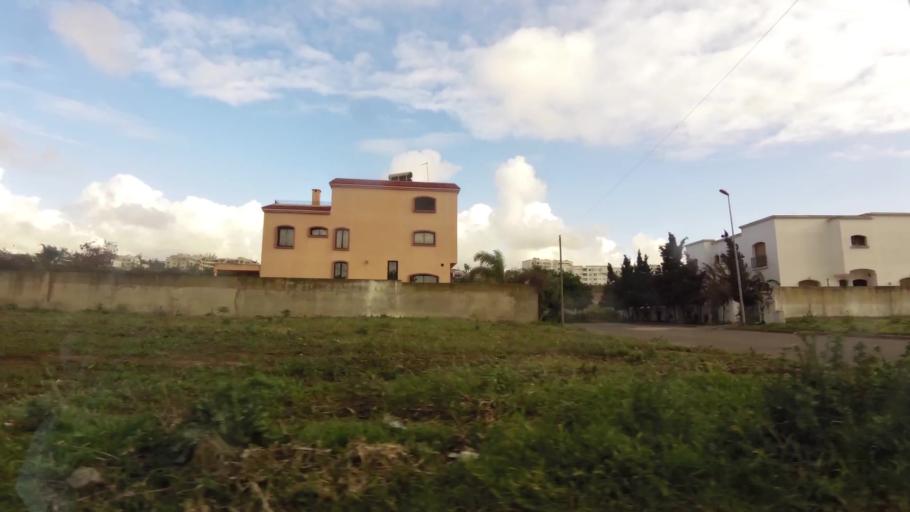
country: MA
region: Grand Casablanca
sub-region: Casablanca
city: Casablanca
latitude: 33.5762
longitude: -7.6936
